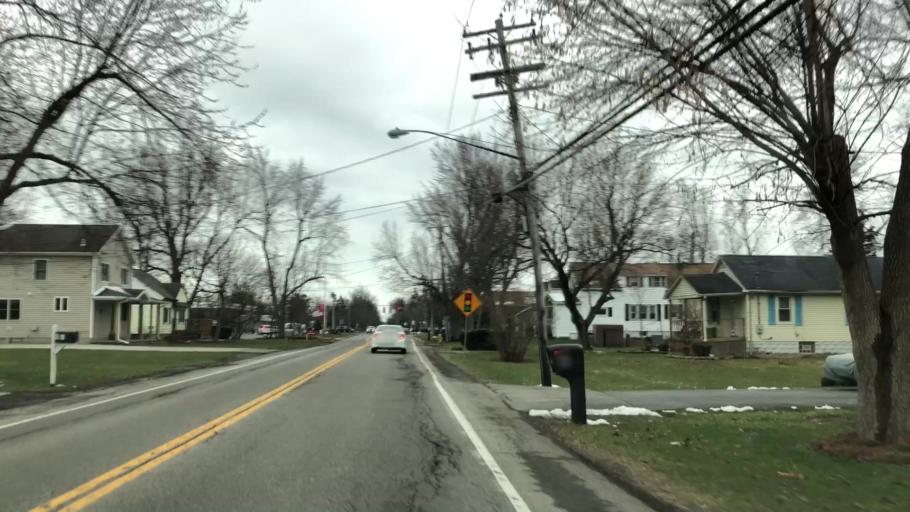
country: US
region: New York
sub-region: Erie County
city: Lancaster
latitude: 42.8825
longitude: -78.6768
